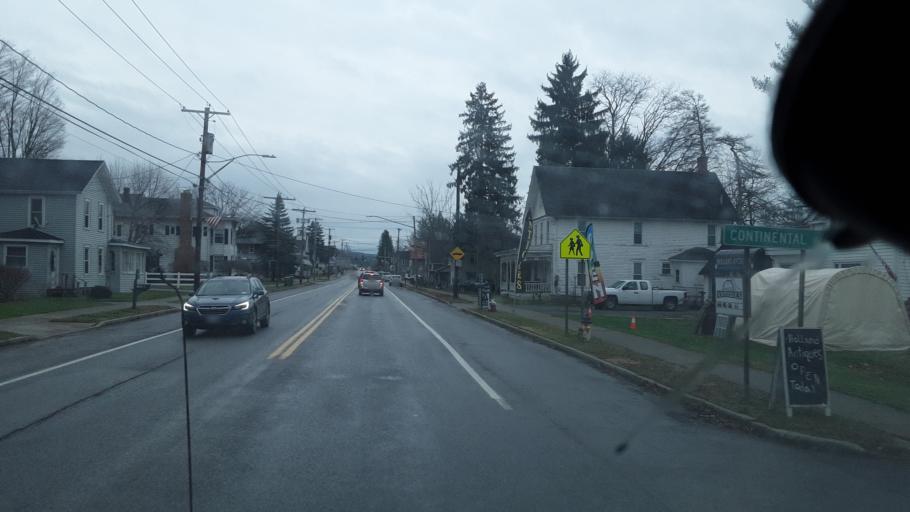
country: US
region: New York
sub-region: Erie County
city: Holland
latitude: 42.6431
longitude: -78.5451
